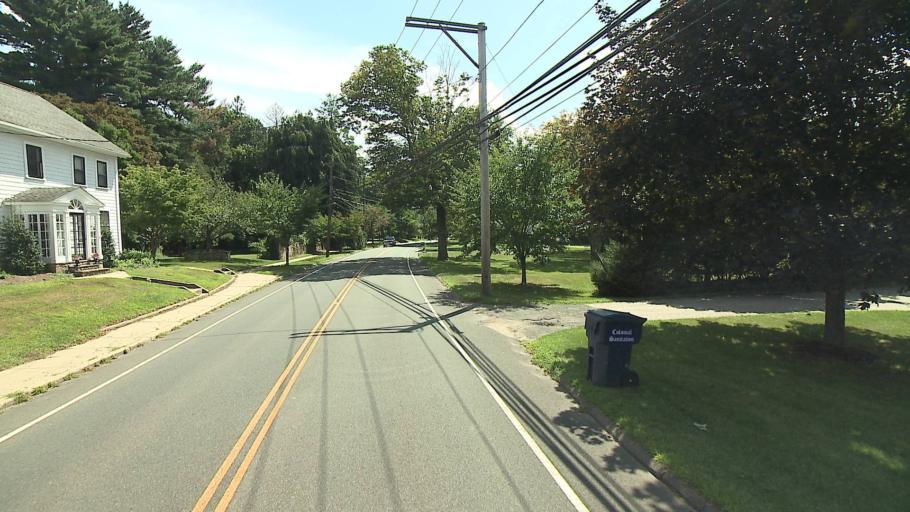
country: US
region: Connecticut
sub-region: Fairfield County
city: Trumbull
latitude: 41.2451
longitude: -73.1617
